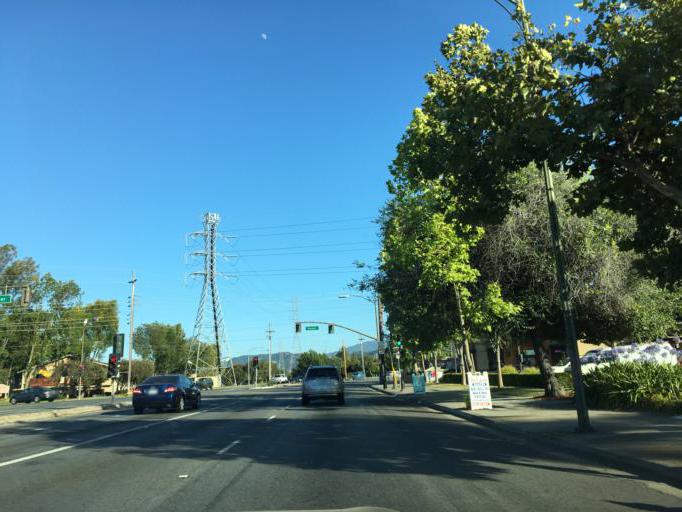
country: US
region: California
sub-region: Santa Clara County
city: Cambrian Park
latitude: 37.2406
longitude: -121.9043
